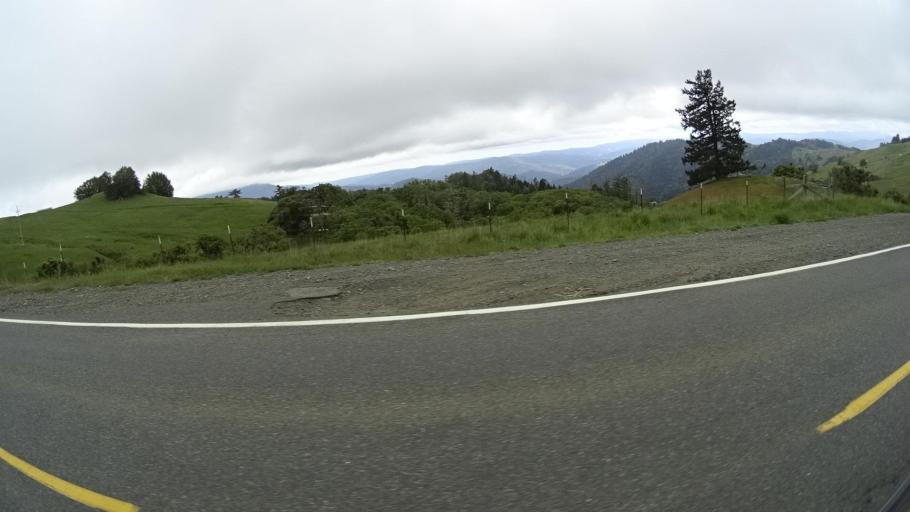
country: US
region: California
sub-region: Humboldt County
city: Redway
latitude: 40.1085
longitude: -123.7158
